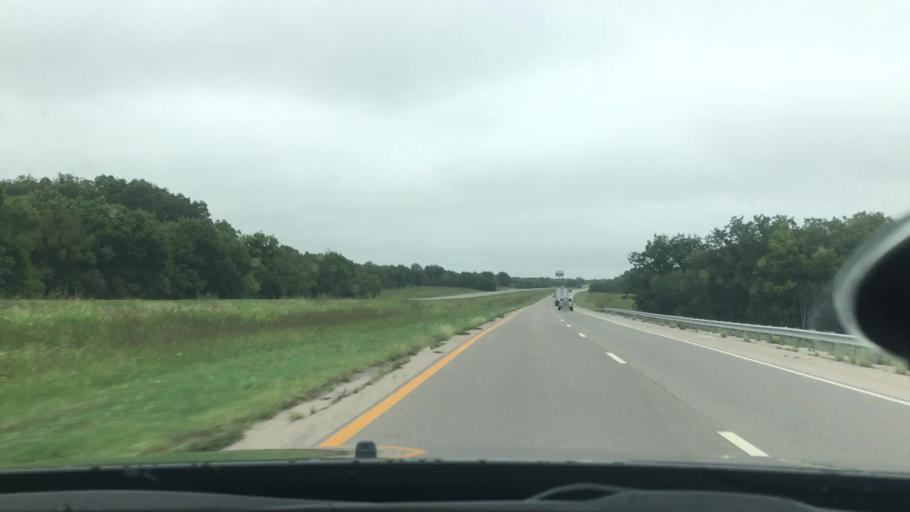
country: US
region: Oklahoma
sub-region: Okfuskee County
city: Okemah
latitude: 35.4275
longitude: -96.2581
